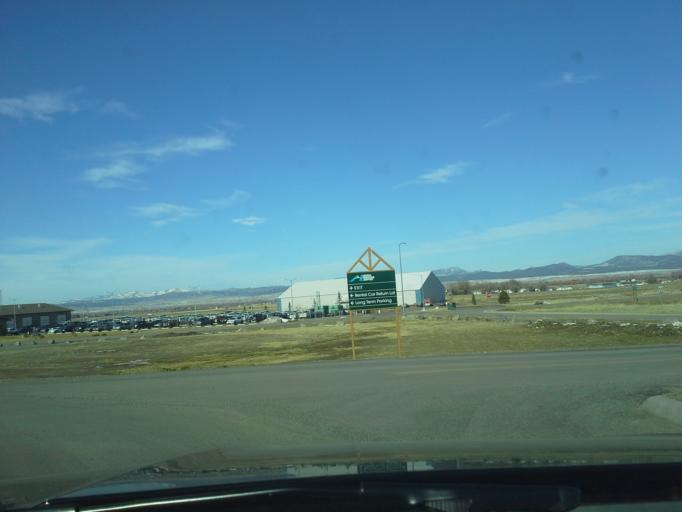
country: US
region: Montana
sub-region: Lewis and Clark County
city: Helena
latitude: 46.6107
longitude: -111.9868
